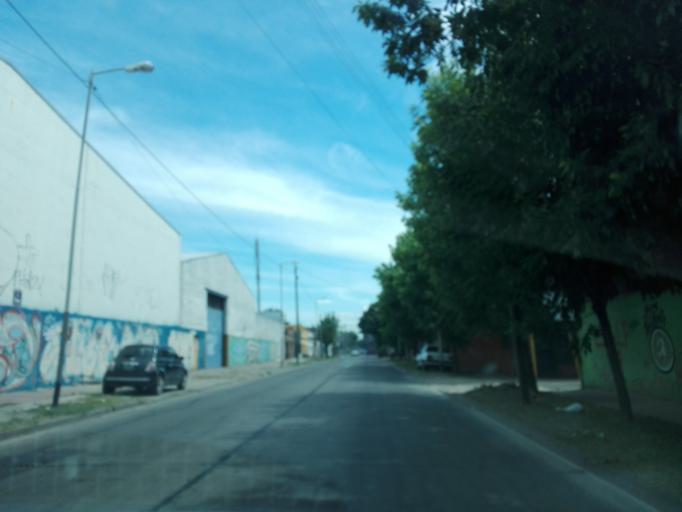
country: AR
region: Buenos Aires
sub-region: Partido de Avellaneda
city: Avellaneda
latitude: -34.6913
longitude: -58.3545
